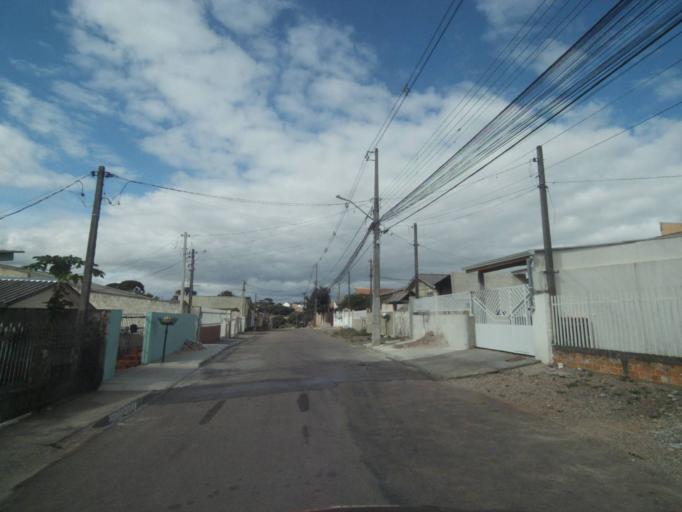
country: BR
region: Parana
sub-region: Sao Jose Dos Pinhais
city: Sao Jose dos Pinhais
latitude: -25.5499
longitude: -49.2488
